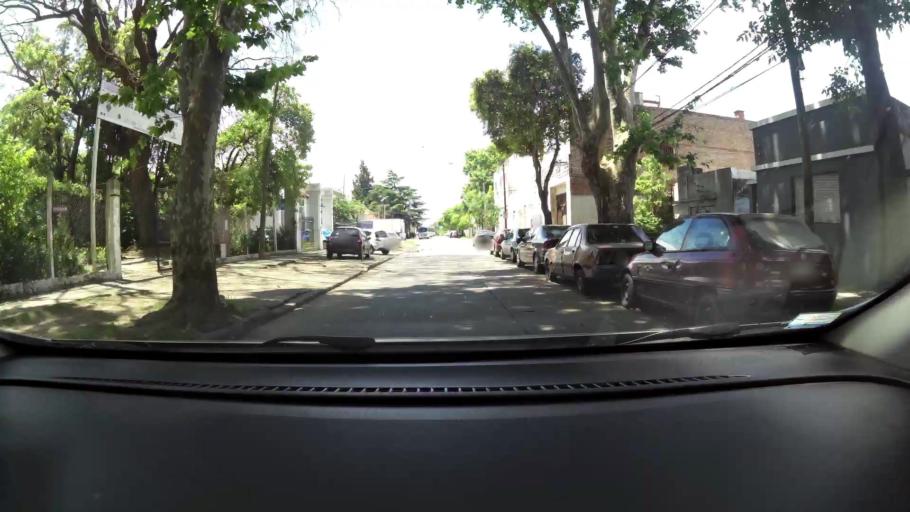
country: AR
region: Santa Fe
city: Gobernador Galvez
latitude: -32.9964
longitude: -60.6243
